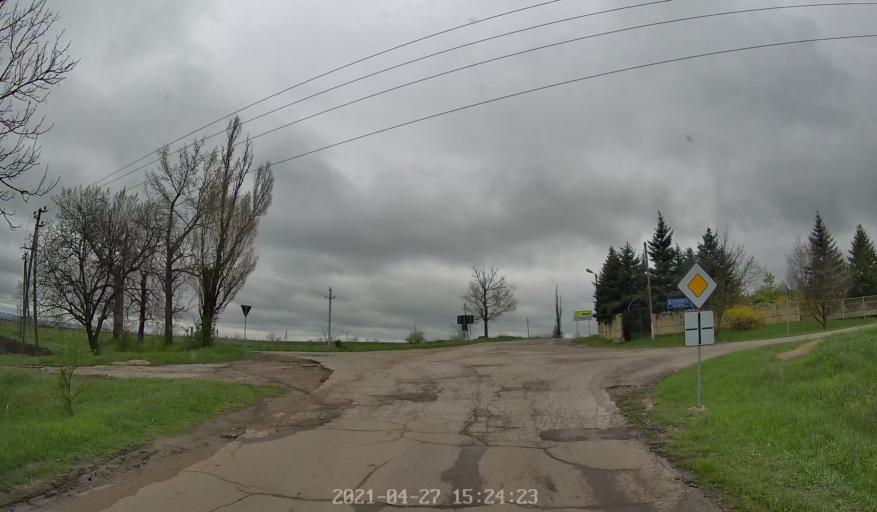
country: MD
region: Chisinau
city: Vadul lui Voda
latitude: 47.0146
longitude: 29.0239
